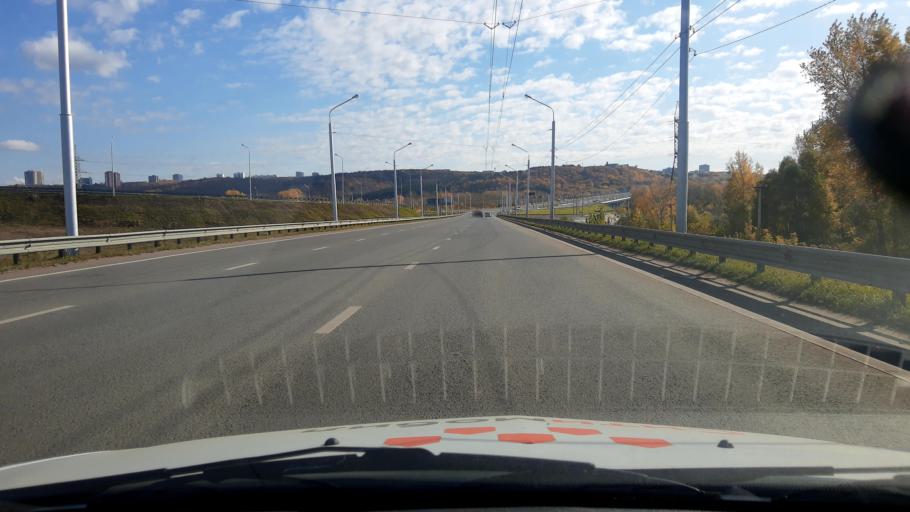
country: RU
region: Bashkortostan
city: Ufa
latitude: 54.7637
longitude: 55.9521
